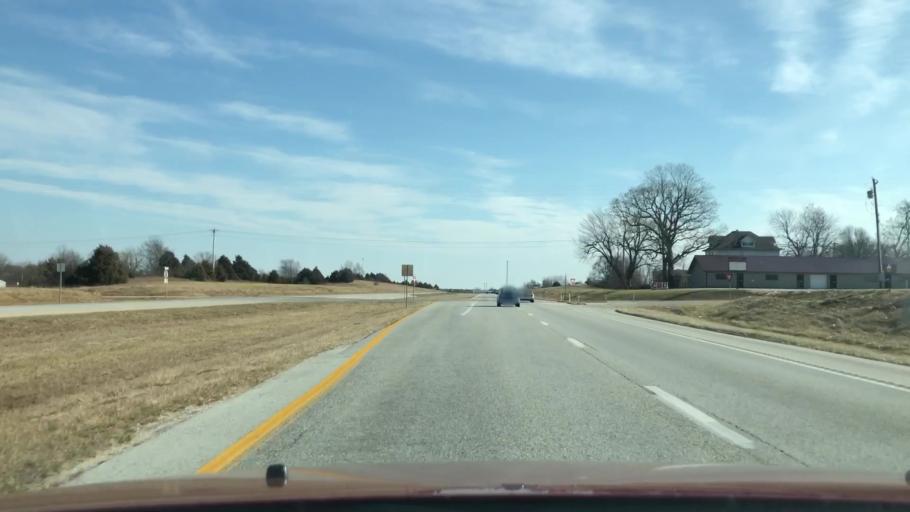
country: US
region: Missouri
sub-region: Webster County
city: Seymour
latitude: 37.1564
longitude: -92.7736
